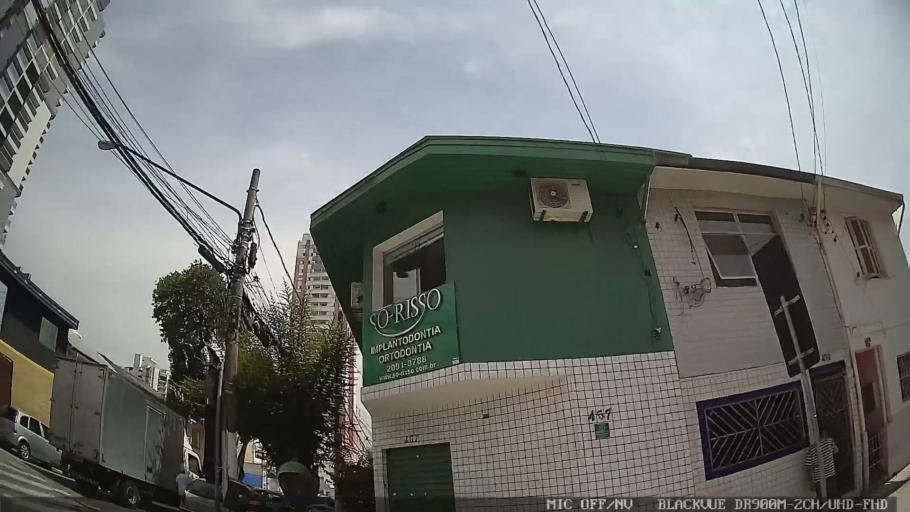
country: BR
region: Sao Paulo
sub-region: Sao Paulo
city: Sao Paulo
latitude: -23.5440
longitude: -46.5714
